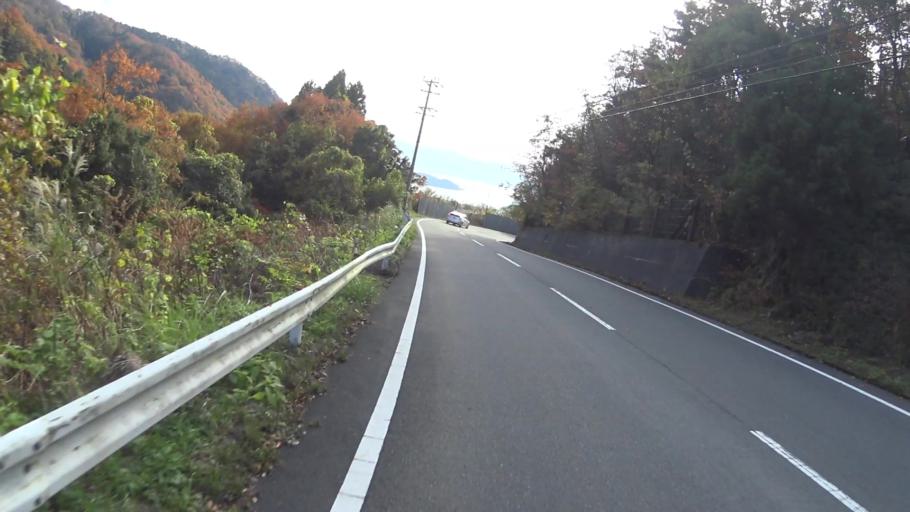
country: JP
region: Kyoto
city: Maizuru
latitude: 35.5316
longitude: 135.3939
